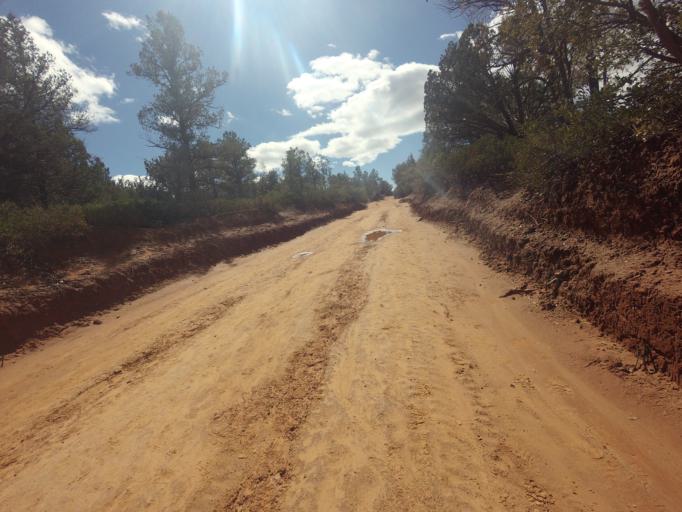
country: US
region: Arizona
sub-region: Yavapai County
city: West Sedona
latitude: 34.9027
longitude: -111.8147
